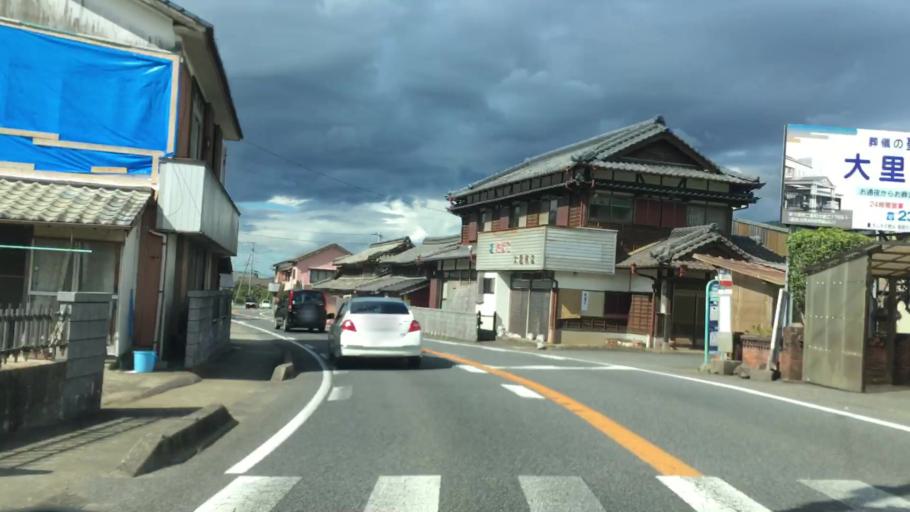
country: JP
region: Saga Prefecture
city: Imaricho-ko
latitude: 33.2289
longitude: 129.8488
